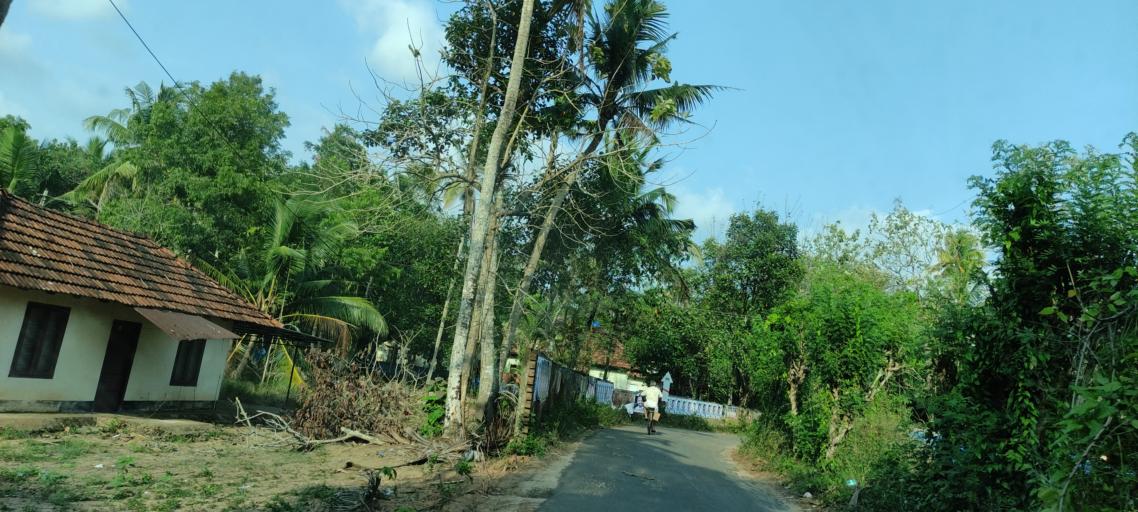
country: IN
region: Kerala
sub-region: Alappuzha
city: Vayalar
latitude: 9.7286
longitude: 76.3090
